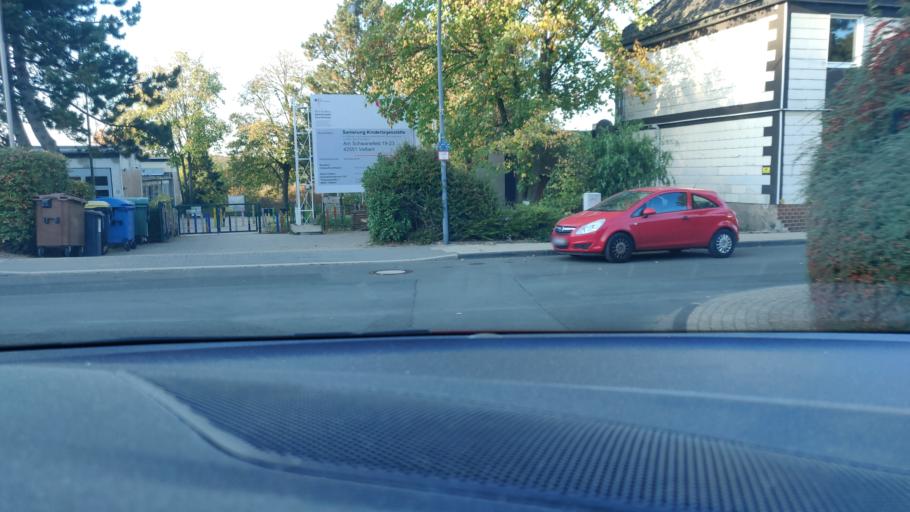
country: DE
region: North Rhine-Westphalia
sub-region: Regierungsbezirk Dusseldorf
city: Velbert
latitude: 51.3510
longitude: 7.0471
